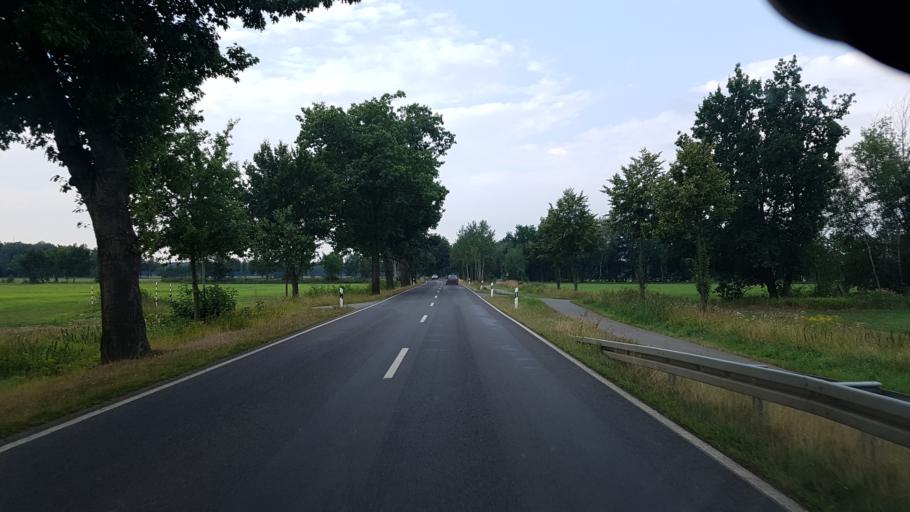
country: DE
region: Brandenburg
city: Tettau
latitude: 51.4585
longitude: 13.7394
